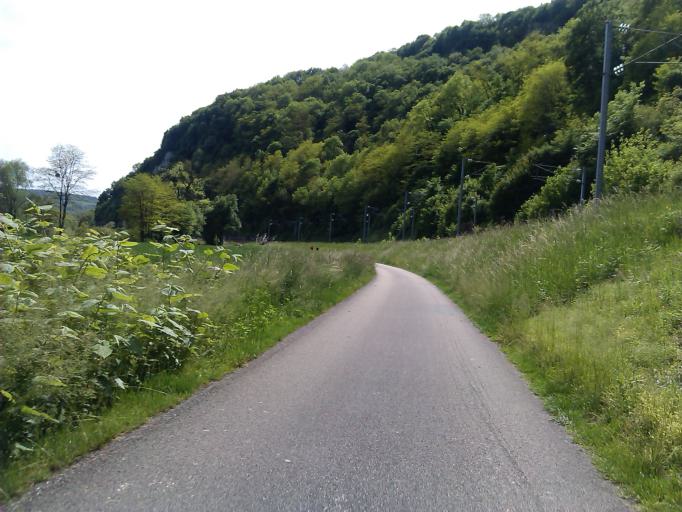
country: FR
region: Franche-Comte
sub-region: Departement du Doubs
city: Boussieres
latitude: 47.1614
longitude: 5.8829
